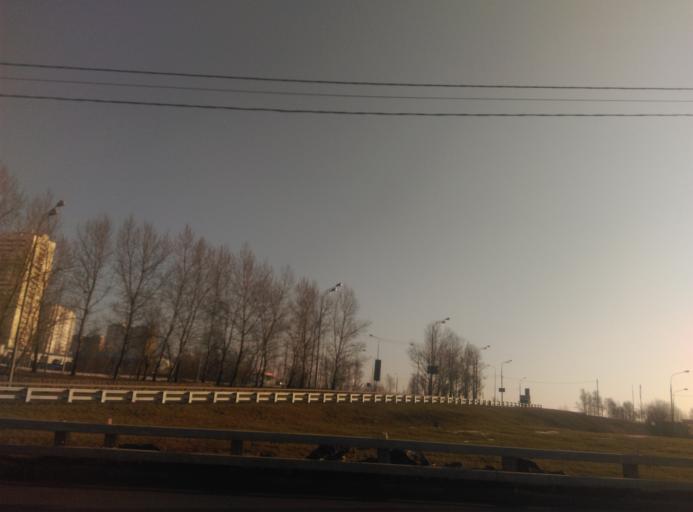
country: RU
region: Moscow
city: Biryulevo
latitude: 55.5775
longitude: 37.6863
